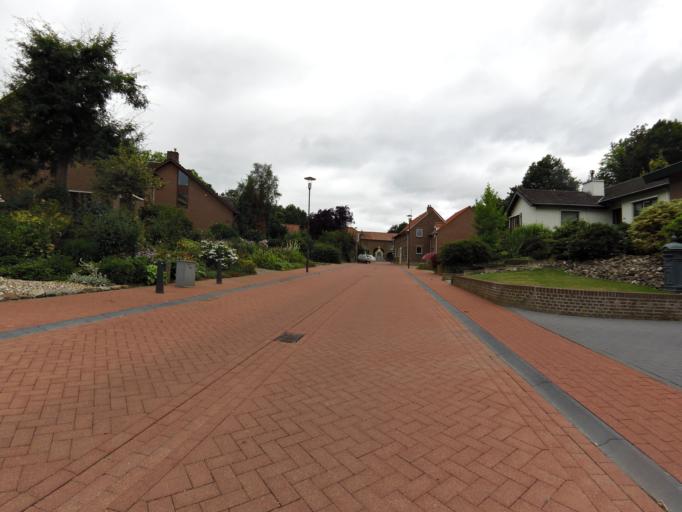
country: NL
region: Limburg
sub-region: Gemeente Nuth
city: Nuth
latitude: 50.9192
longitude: 5.8630
